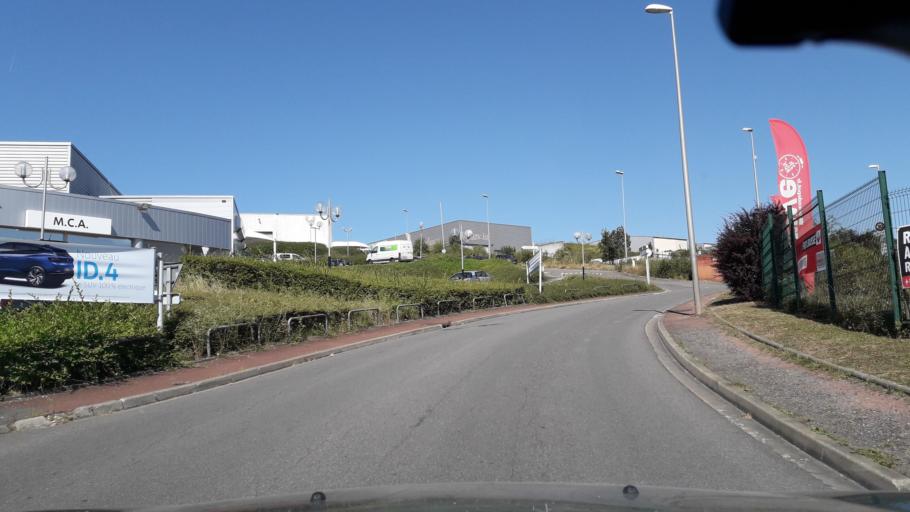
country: FR
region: Poitou-Charentes
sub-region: Departement de la Charente
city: Gond-Pontouvre
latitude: 45.6858
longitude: 0.1819
